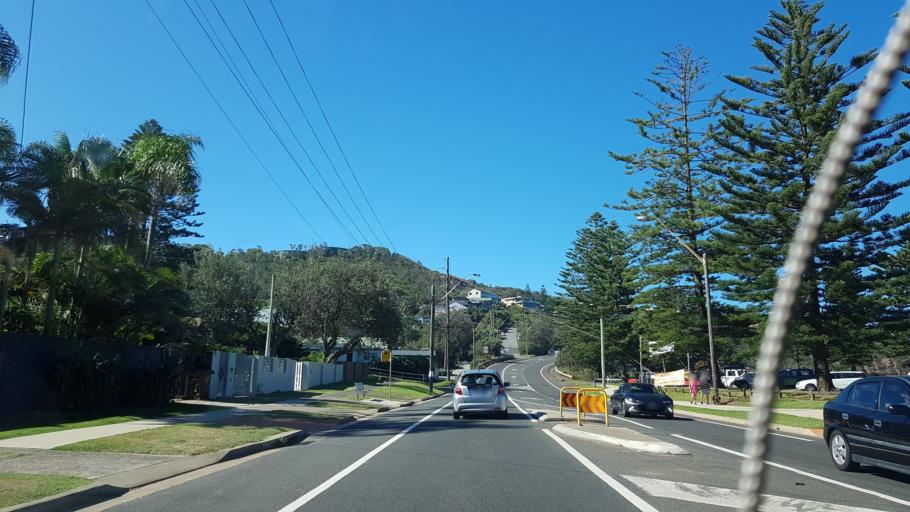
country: AU
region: New South Wales
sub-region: Pittwater
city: Newport
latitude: -33.6522
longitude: 151.3229
